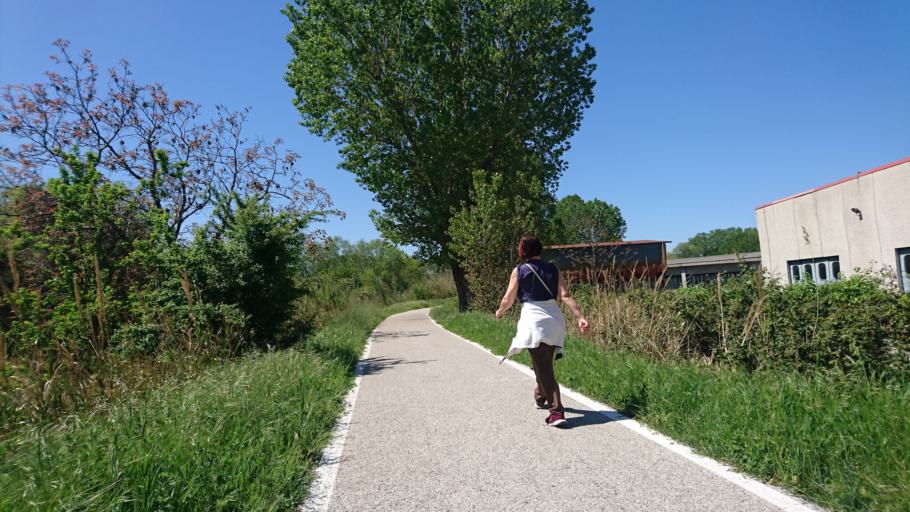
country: IT
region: The Marches
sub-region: Provincia di Pesaro e Urbino
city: Pesaro
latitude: 43.9014
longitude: 12.8866
